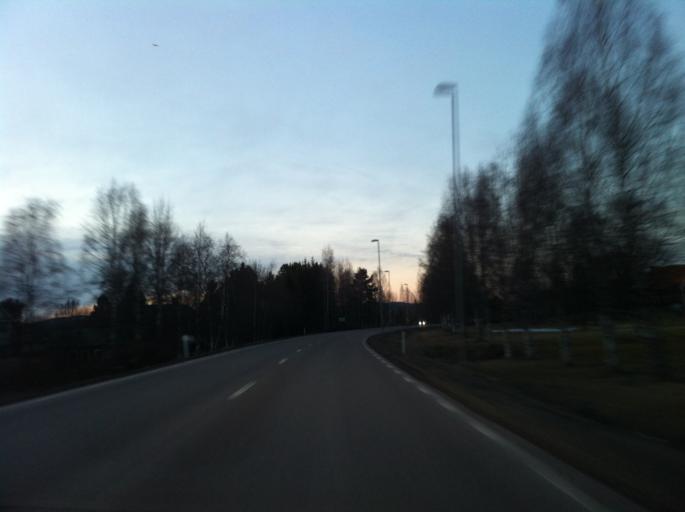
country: SE
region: Dalarna
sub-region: Orsa Kommun
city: Orsa
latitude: 61.1103
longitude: 14.6285
